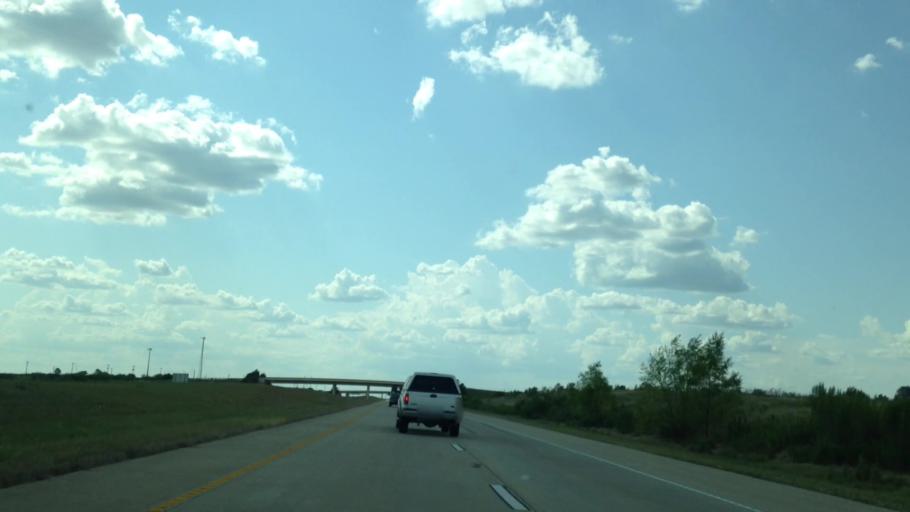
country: US
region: Texas
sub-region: Travis County
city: Onion Creek
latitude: 30.0915
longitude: -97.7502
